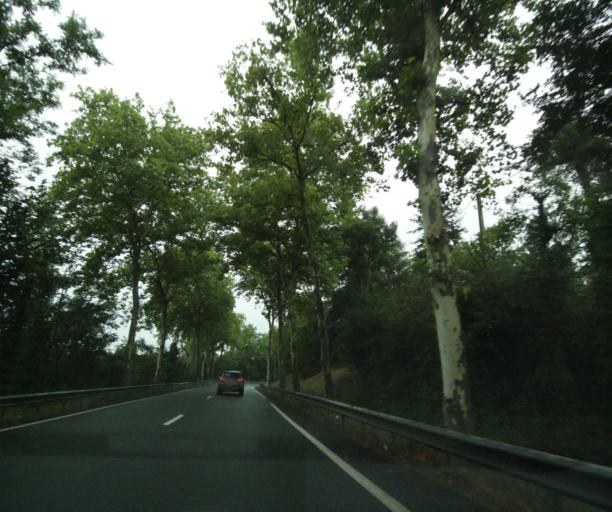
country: FR
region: Midi-Pyrenees
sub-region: Departement du Tarn
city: Le Garric
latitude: 43.9801
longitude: 2.1748
